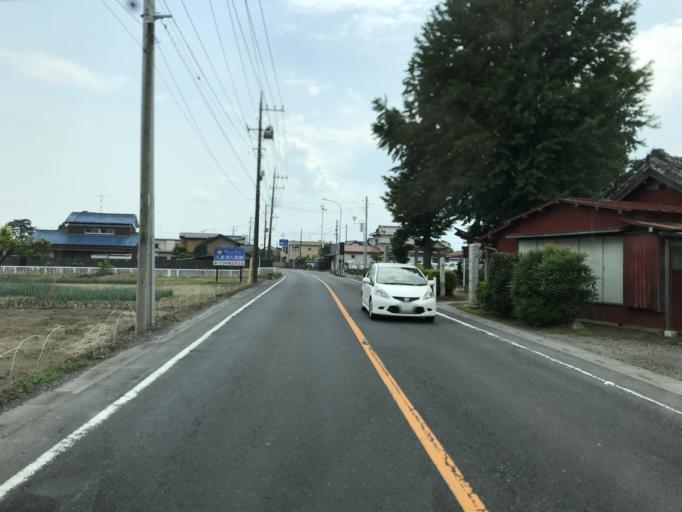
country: JP
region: Saitama
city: Kukichuo
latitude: 36.0848
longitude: 139.6495
